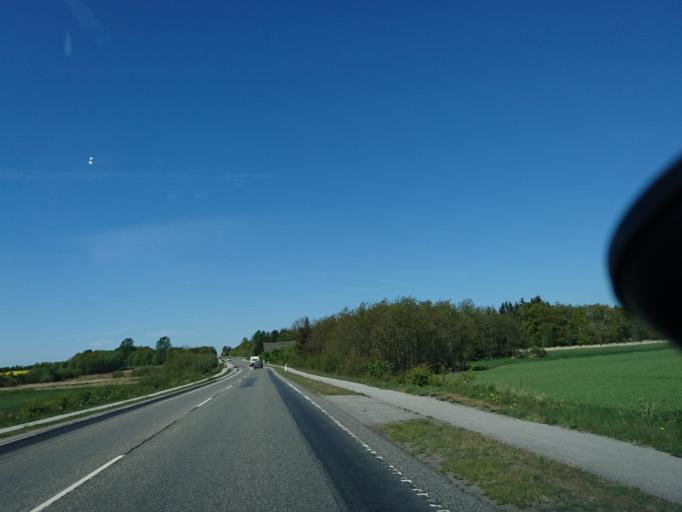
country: DK
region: North Denmark
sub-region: Hjorring Kommune
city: Tars
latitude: 57.4564
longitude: 10.0810
